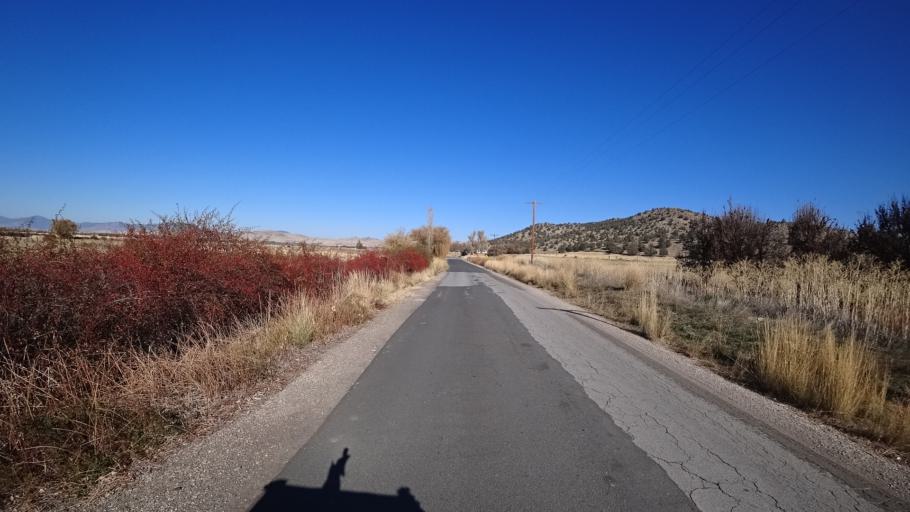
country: US
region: California
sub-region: Siskiyou County
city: Montague
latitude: 41.6997
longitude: -122.3762
